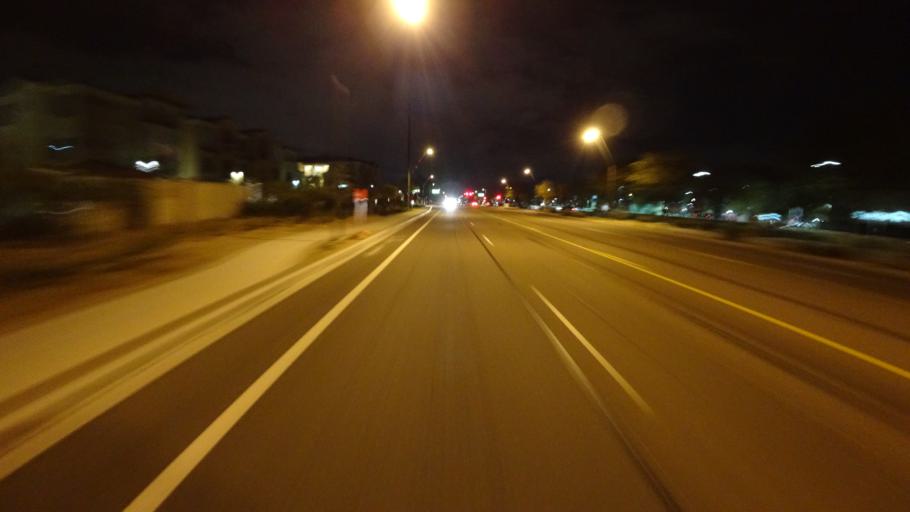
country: US
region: Arizona
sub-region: Maricopa County
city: Guadalupe
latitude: 33.3329
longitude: -111.9632
